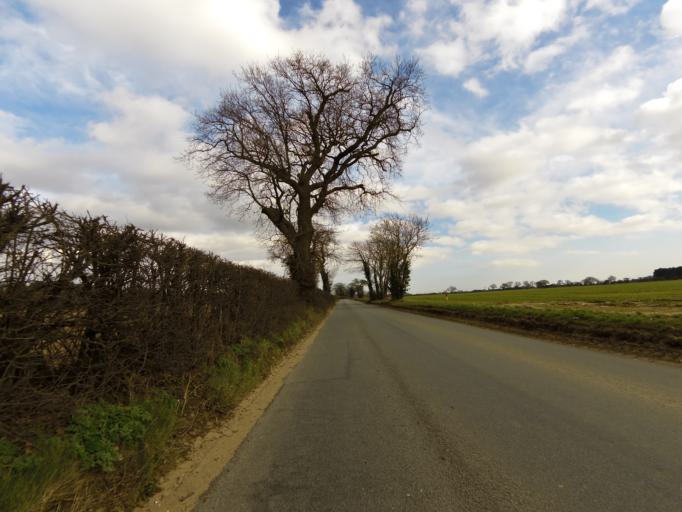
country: GB
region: England
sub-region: Suffolk
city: Kesgrave
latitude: 52.0484
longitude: 1.2812
